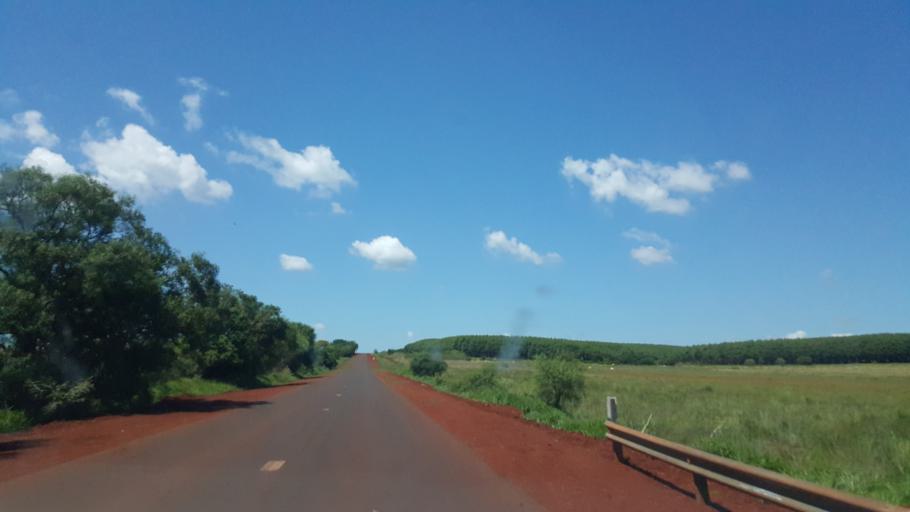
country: AR
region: Corrientes
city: Santo Tome
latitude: -28.3440
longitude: -55.9311
